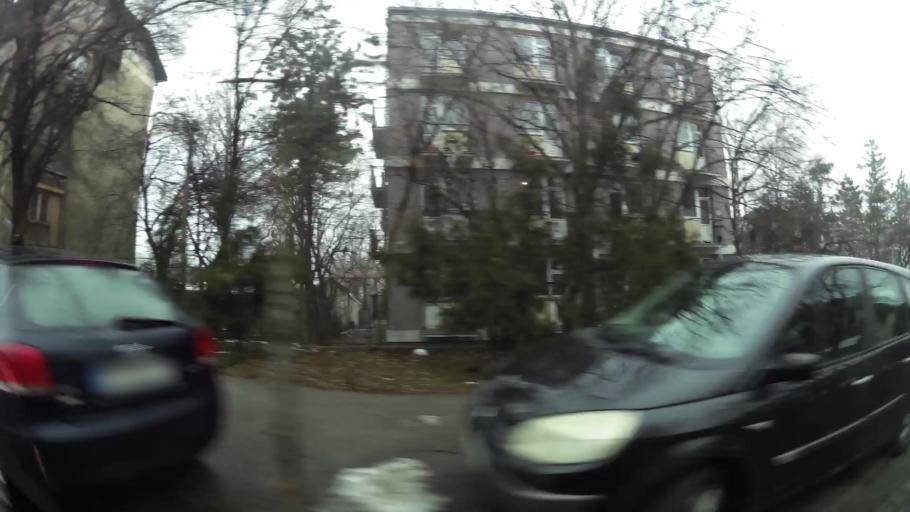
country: RS
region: Central Serbia
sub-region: Belgrade
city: Novi Beograd
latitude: 44.7939
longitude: 20.4390
